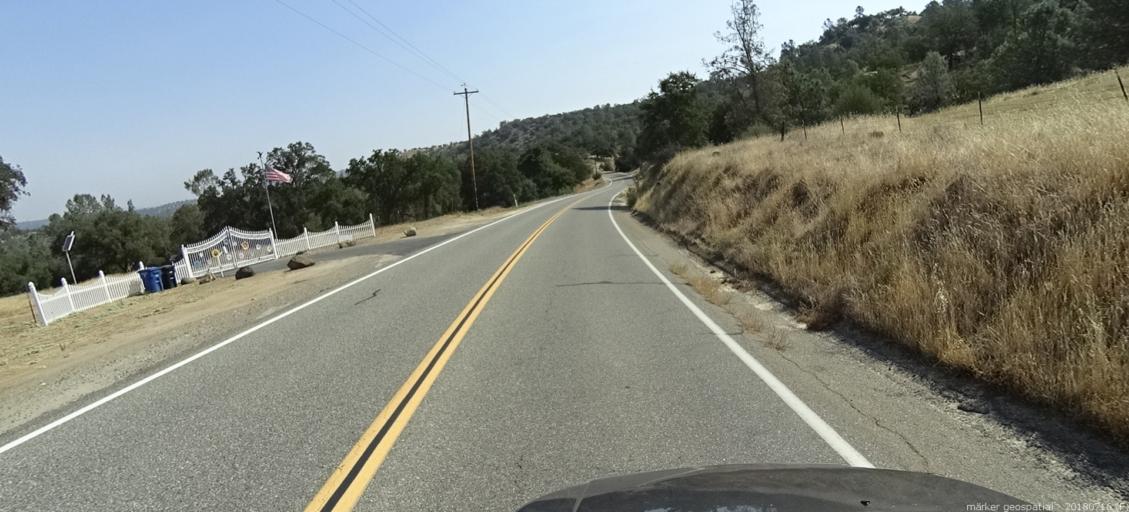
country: US
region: California
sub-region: Madera County
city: Yosemite Lakes
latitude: 37.2088
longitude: -119.7722
